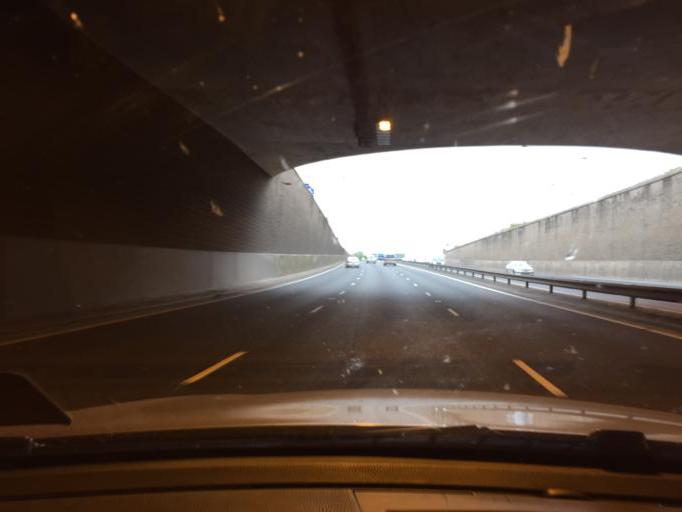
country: GB
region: Northern Ireland
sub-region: City of Belfast
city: Belfast
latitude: 54.5889
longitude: -5.9585
